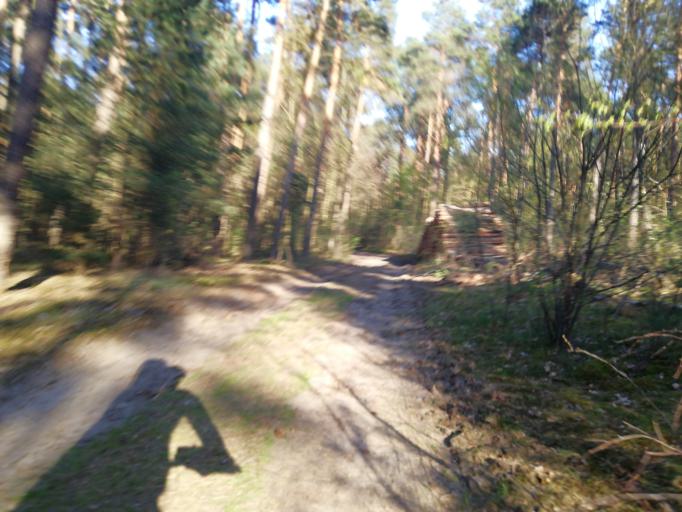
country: DE
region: Brandenburg
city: Calau
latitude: 51.7236
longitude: 13.9616
